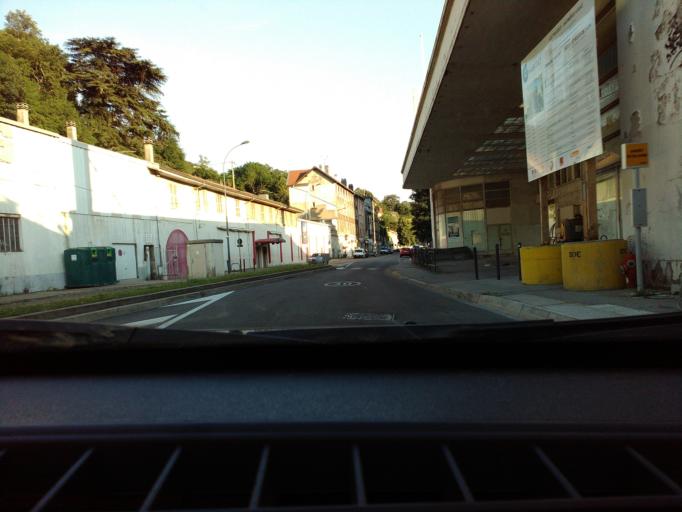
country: FR
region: Rhone-Alpes
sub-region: Departement de l'Isere
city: Saint-Martin-le-Vinoux
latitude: 45.1980
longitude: 5.7182
